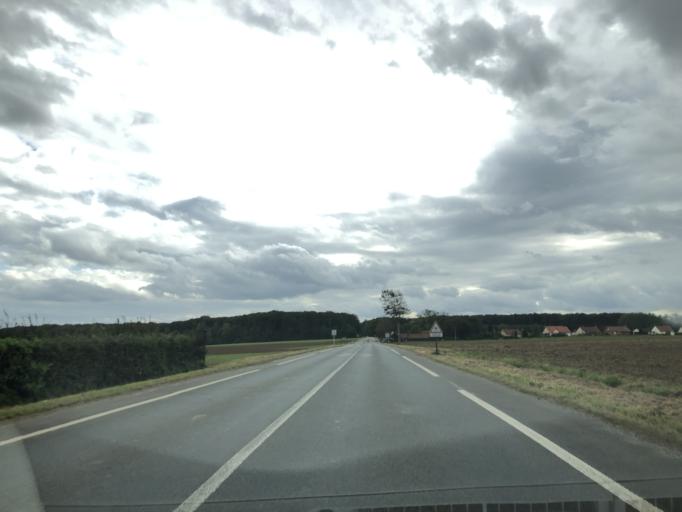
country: FR
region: Nord-Pas-de-Calais
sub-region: Departement du Pas-de-Calais
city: Hesdin
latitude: 50.4142
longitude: 2.0487
